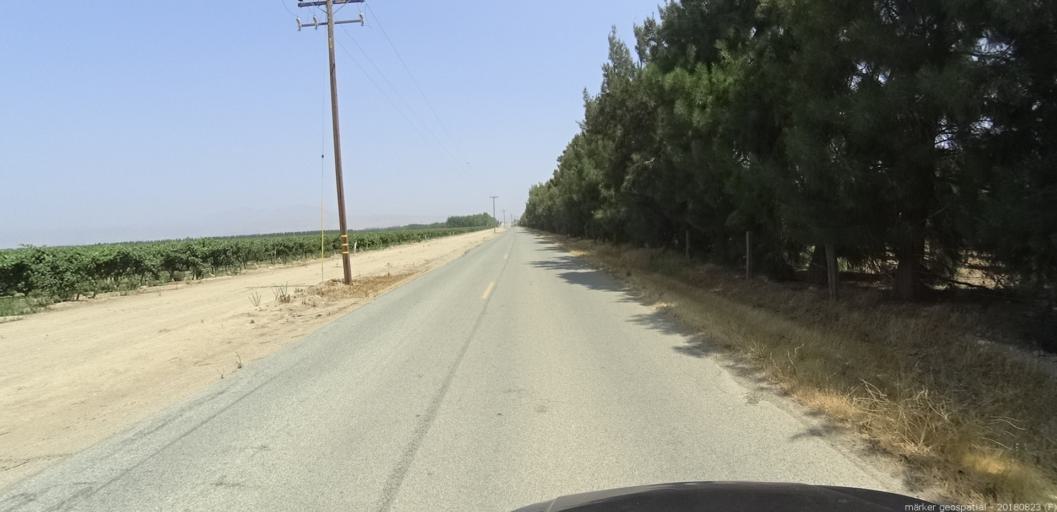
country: US
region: California
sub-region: Monterey County
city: Greenfield
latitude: 36.3196
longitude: -121.3003
